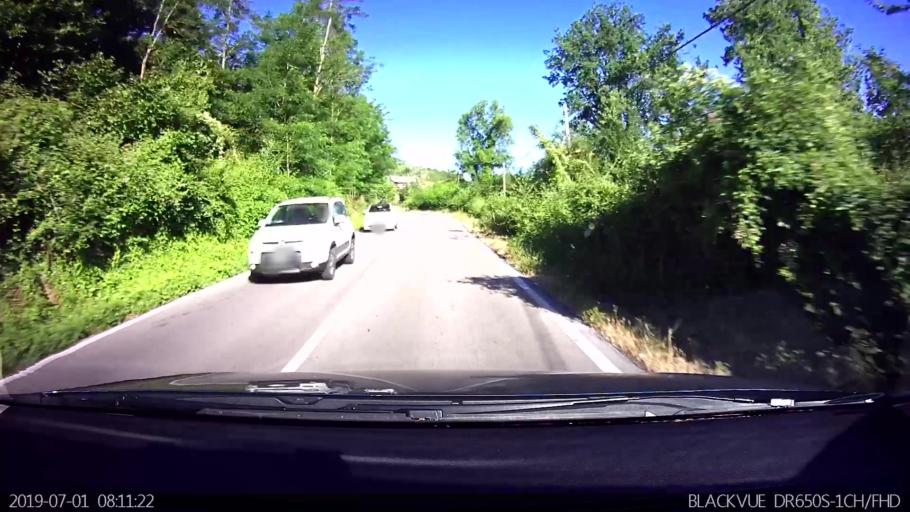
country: IT
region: Latium
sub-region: Provincia di Frosinone
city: Sant'Angelo in Villa-Giglio
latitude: 41.6772
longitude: 13.4204
